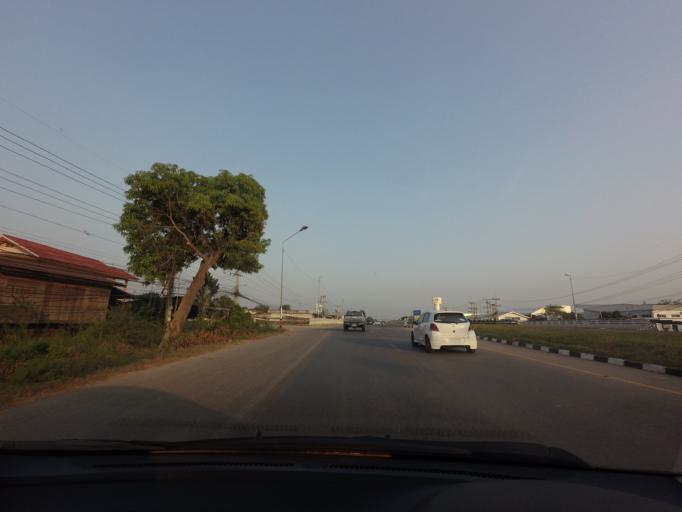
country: TH
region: Sukhothai
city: Sukhothai
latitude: 17.0217
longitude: 99.8192
